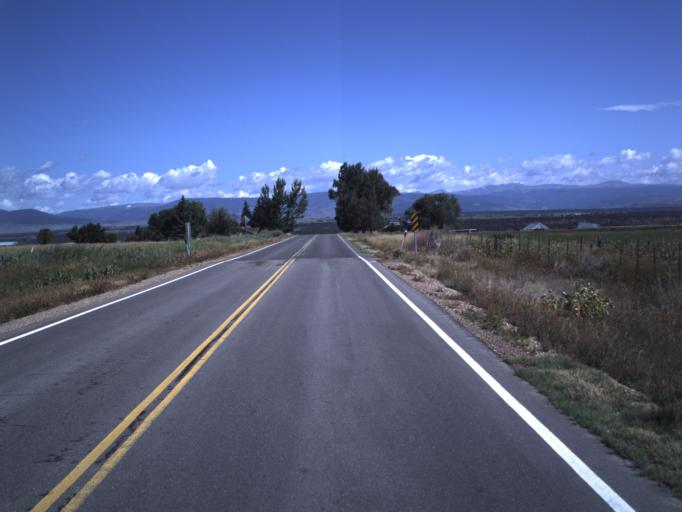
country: US
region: Utah
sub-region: Duchesne County
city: Duchesne
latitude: 40.3282
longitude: -110.4079
